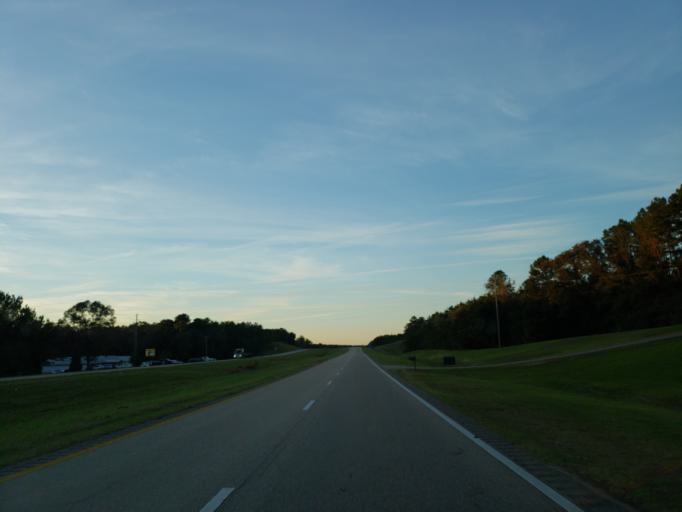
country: US
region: Mississippi
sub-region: Wayne County
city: Belmont
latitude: 31.4770
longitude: -88.4813
